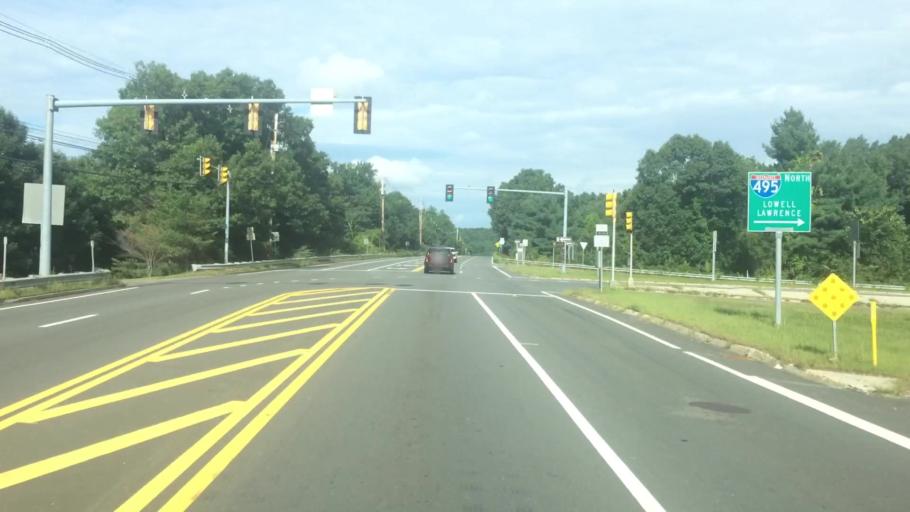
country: US
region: Massachusetts
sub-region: Worcester County
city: Harvard
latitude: 42.4863
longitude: -71.5418
